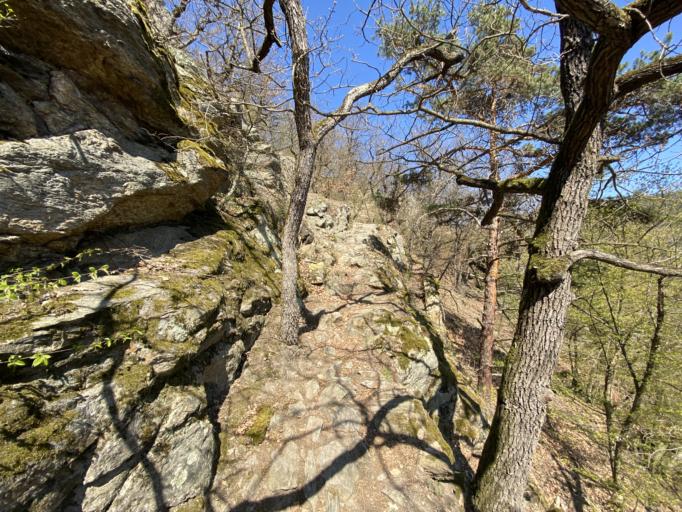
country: AT
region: Lower Austria
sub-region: Politischer Bezirk Krems
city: Durnstein
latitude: 48.4024
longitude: 15.5192
